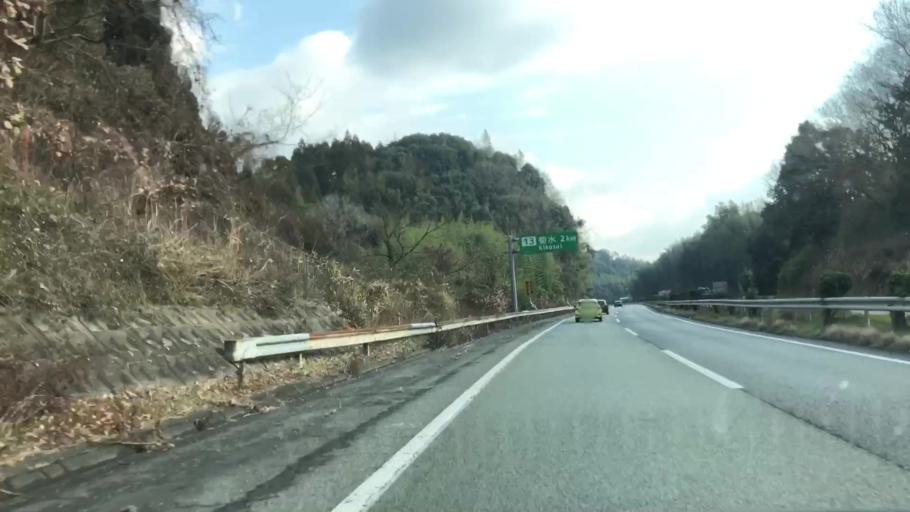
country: JP
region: Kumamoto
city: Tamana
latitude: 33.0004
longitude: 130.5901
